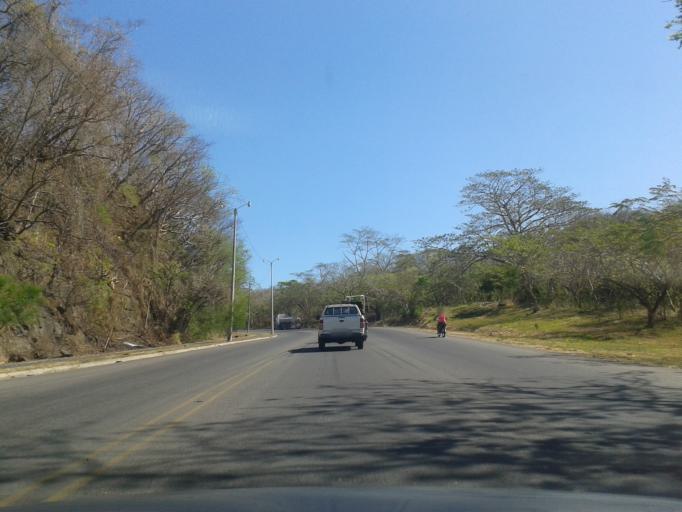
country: CR
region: Puntarenas
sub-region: Canton Central de Puntarenas
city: Chacarita
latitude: 9.9422
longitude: -84.7280
